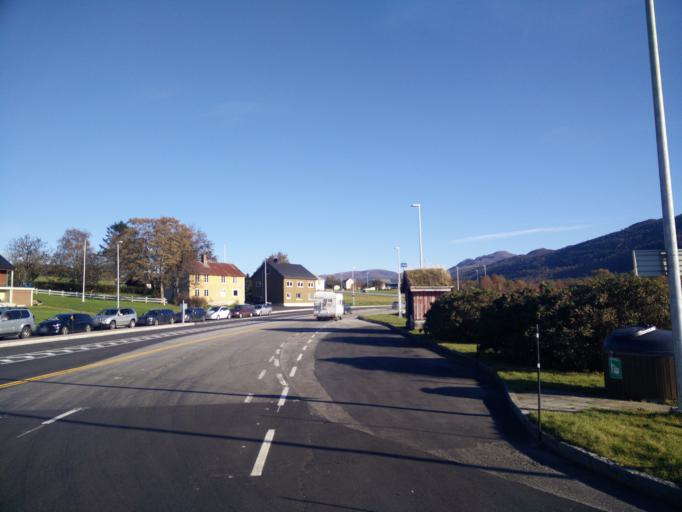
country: NO
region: More og Romsdal
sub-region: Halsa
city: Liaboen
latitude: 63.0683
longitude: 8.2275
